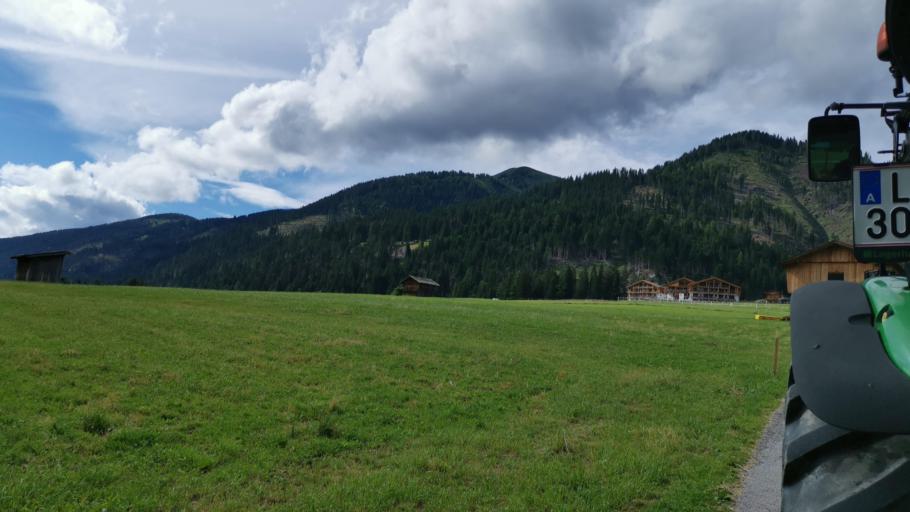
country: AT
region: Tyrol
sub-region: Politischer Bezirk Lienz
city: Obertilliach
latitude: 46.7059
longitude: 12.6113
